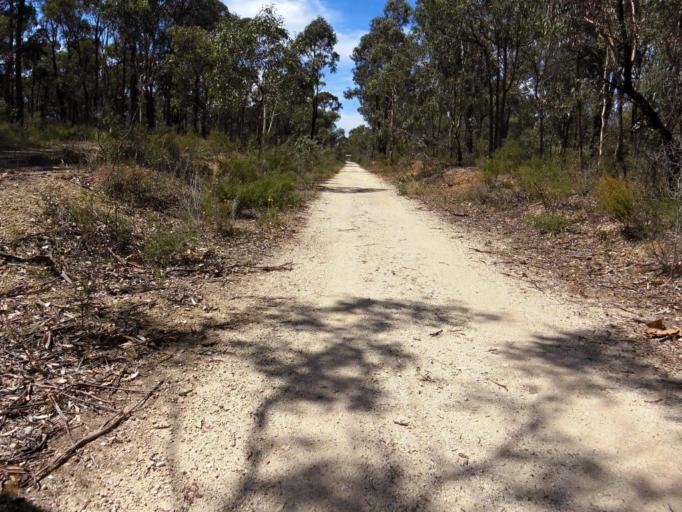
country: AU
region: Victoria
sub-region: Greater Bendigo
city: Kennington
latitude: -36.7603
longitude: 144.3357
